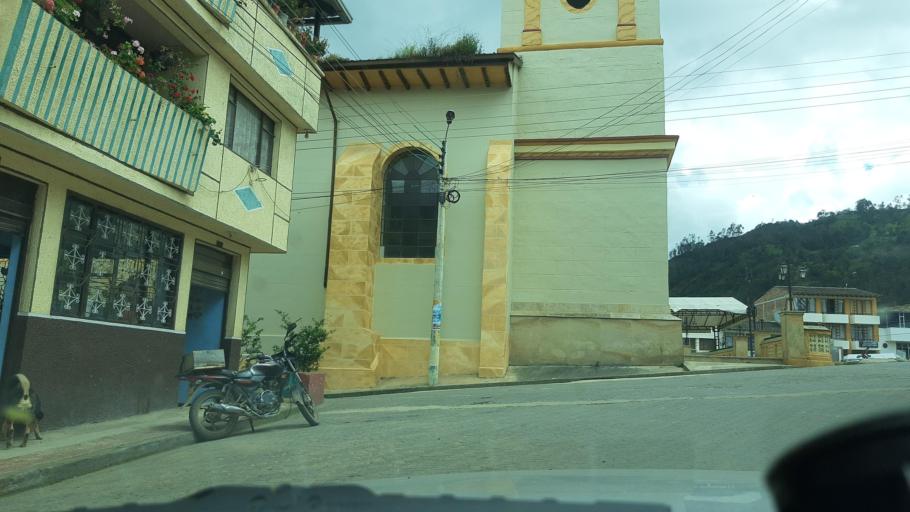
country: CO
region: Cundinamarca
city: Umbita
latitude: 5.2210
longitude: -73.4565
